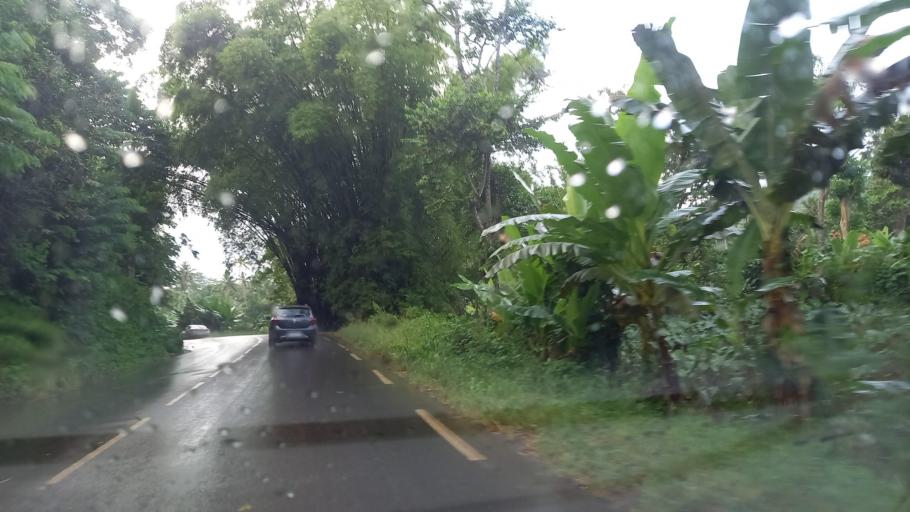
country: YT
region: Ouangani
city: Ouangani
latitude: -12.8365
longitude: 45.1430
